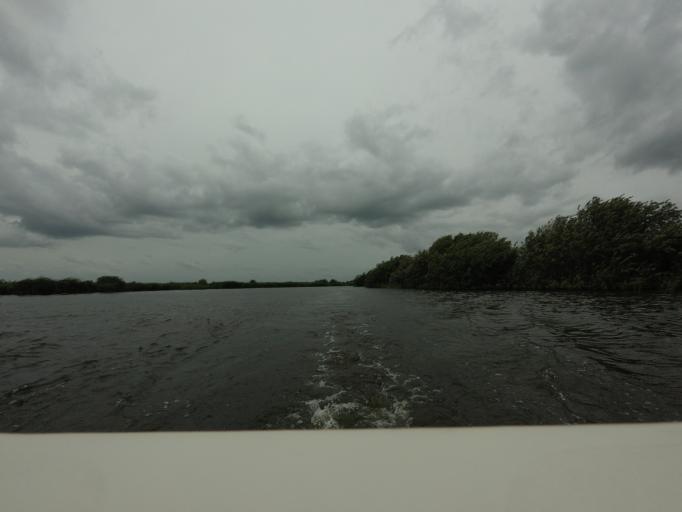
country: NL
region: Friesland
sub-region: Gemeente Boarnsterhim
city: Aldeboarn
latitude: 53.0966
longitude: 5.9201
